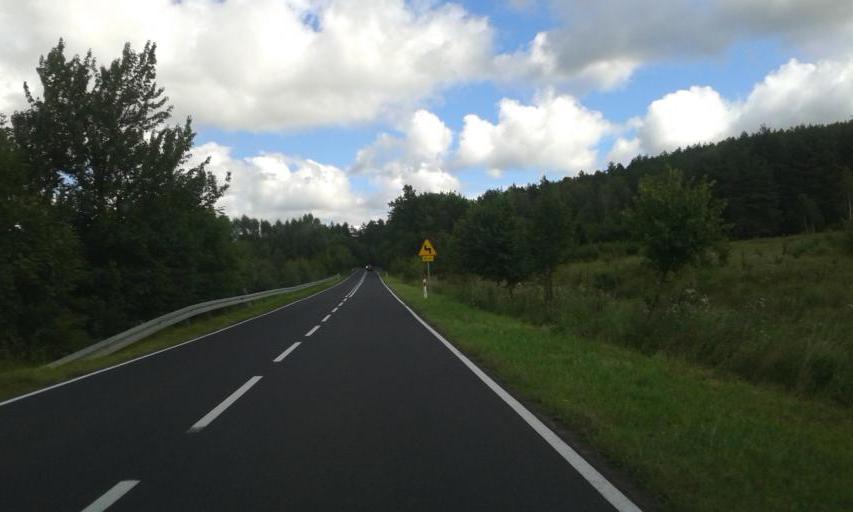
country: PL
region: West Pomeranian Voivodeship
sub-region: Powiat koszalinski
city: Polanow
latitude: 54.0100
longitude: 16.7174
